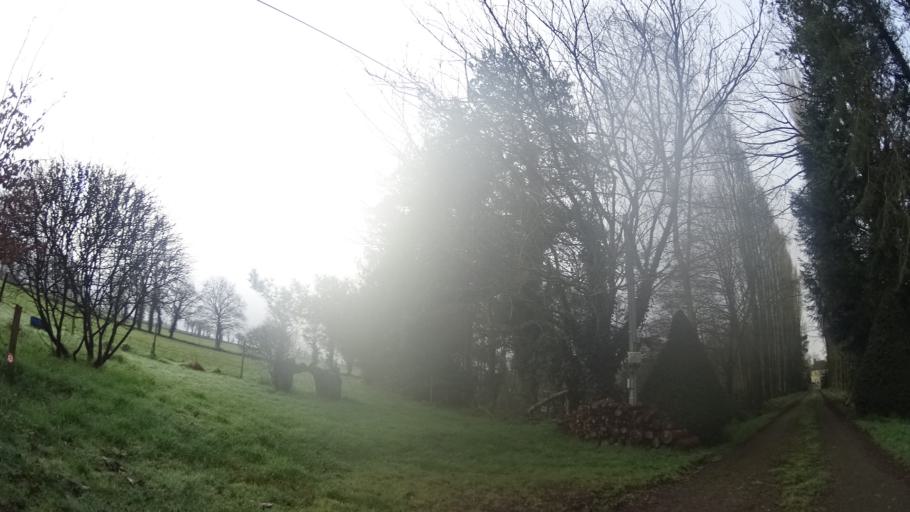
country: FR
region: Brittany
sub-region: Departement des Cotes-d'Armor
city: Evran
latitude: 48.3299
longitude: -1.9429
